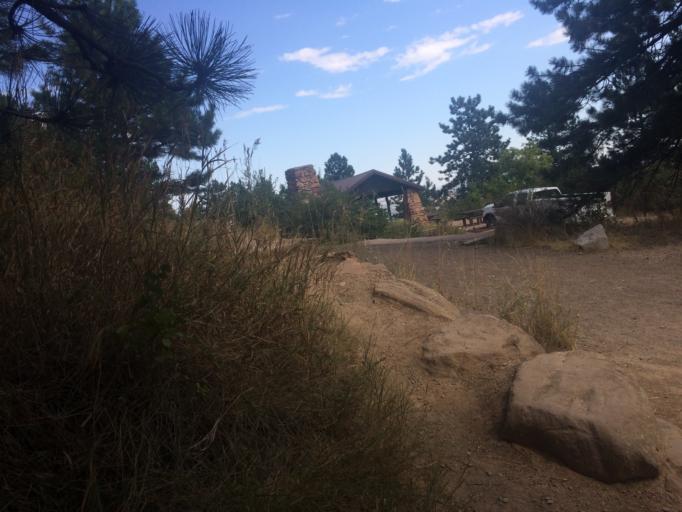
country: US
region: Colorado
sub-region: Boulder County
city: Boulder
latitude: 39.9910
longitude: -105.2875
